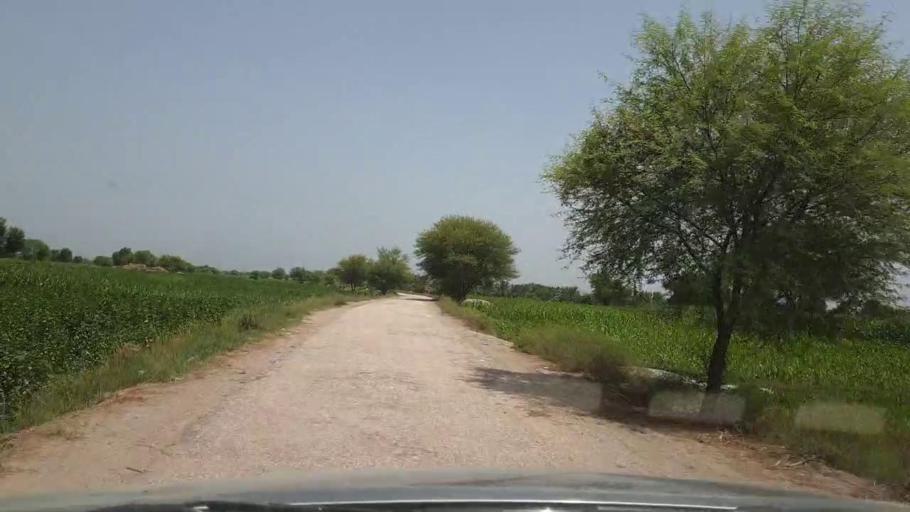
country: PK
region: Sindh
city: Pano Aqil
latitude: 27.8317
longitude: 69.1929
